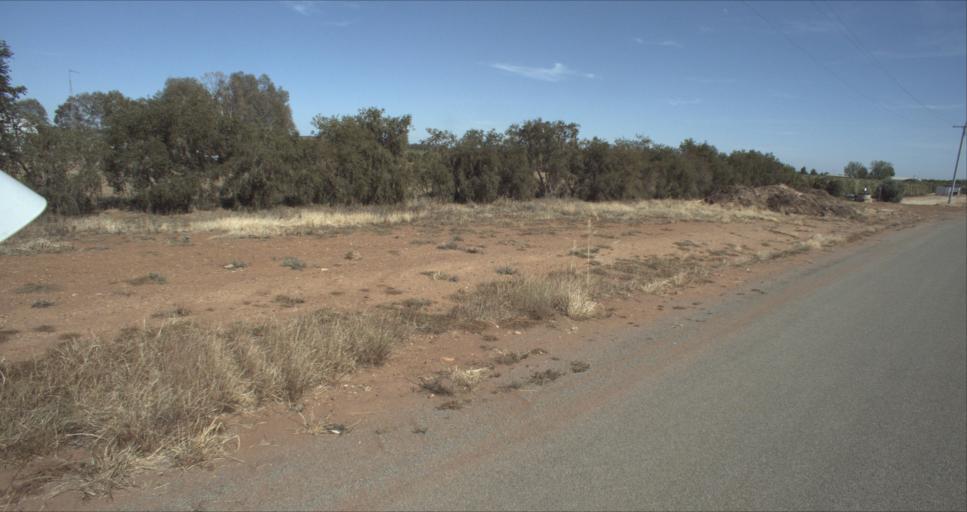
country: AU
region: New South Wales
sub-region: Leeton
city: Leeton
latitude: -34.5775
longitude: 146.4779
